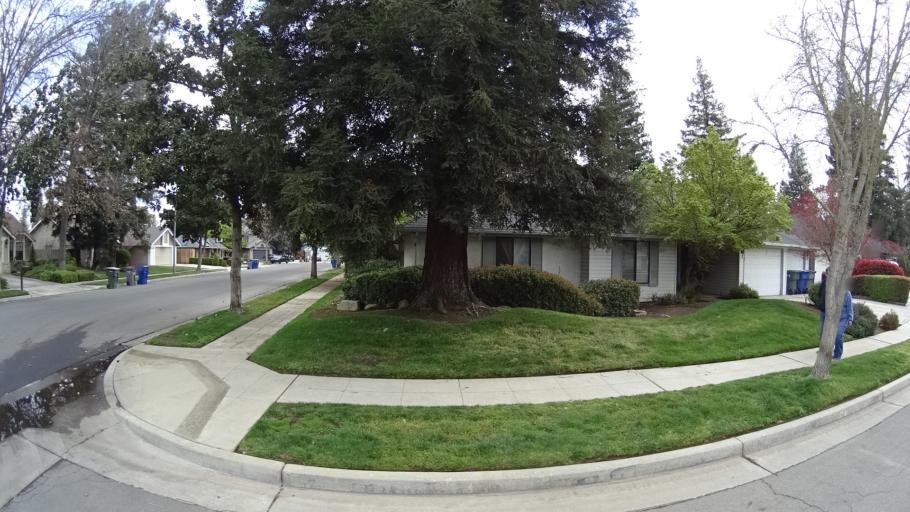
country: US
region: California
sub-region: Fresno County
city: Fresno
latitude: 36.8332
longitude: -119.8115
